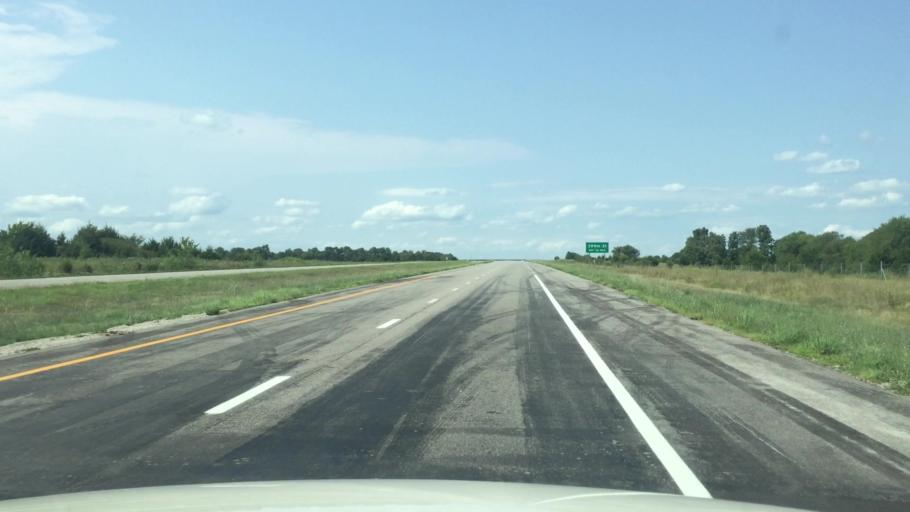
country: US
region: Kansas
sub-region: Linn County
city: La Cygne
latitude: 38.3890
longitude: -94.6874
